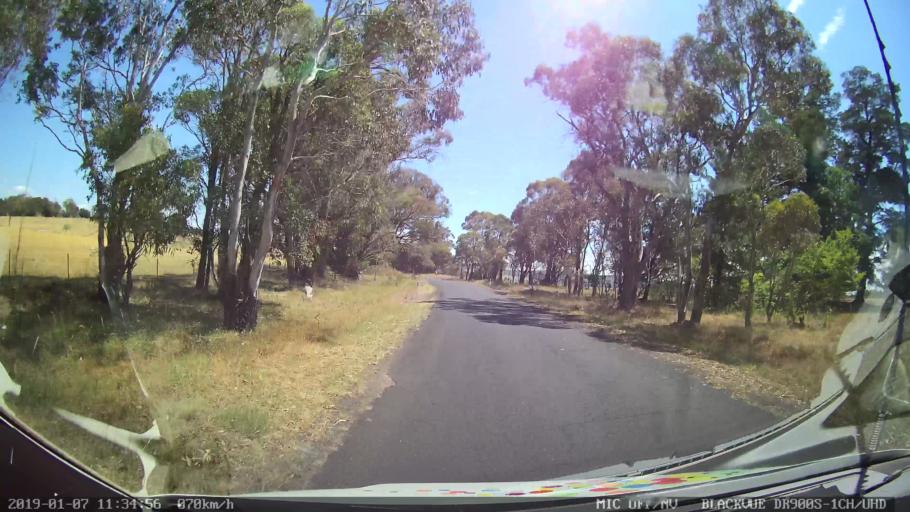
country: AU
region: New South Wales
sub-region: Armidale Dumaresq
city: Armidale
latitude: -30.3853
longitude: 151.5575
